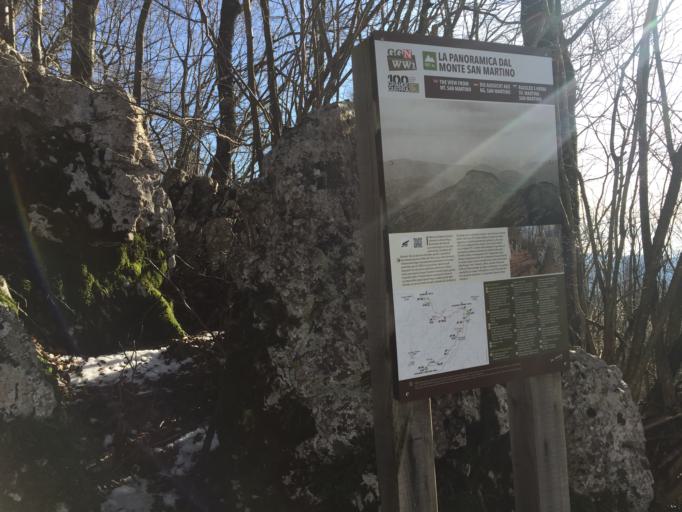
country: IT
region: Friuli Venezia Giulia
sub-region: Provincia di Udine
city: Clodig
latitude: 46.1719
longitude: 13.5860
